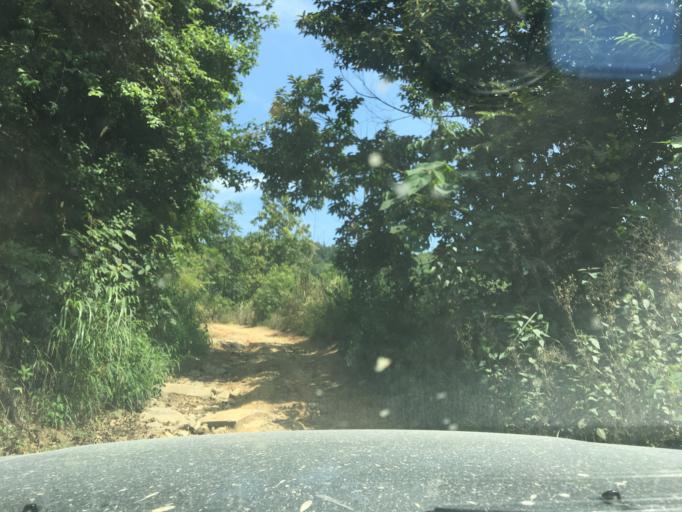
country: CN
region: Guangxi Zhuangzu Zizhiqu
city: Xinzhou
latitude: 25.0462
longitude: 105.8600
